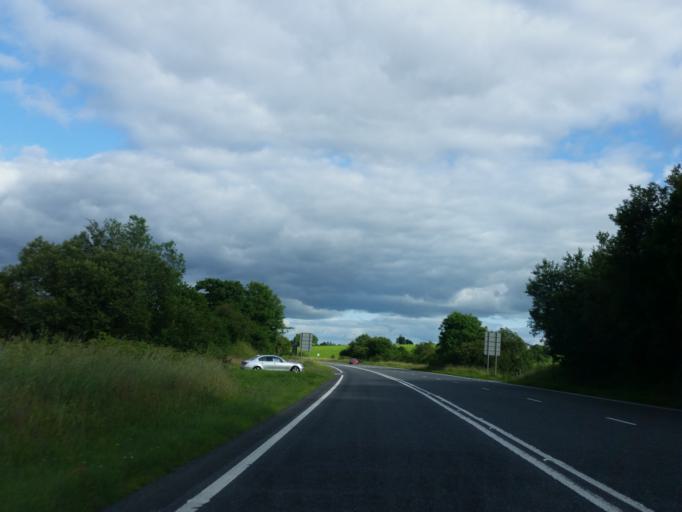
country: GB
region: Northern Ireland
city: Lisnaskea
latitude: 54.3066
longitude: -7.4907
